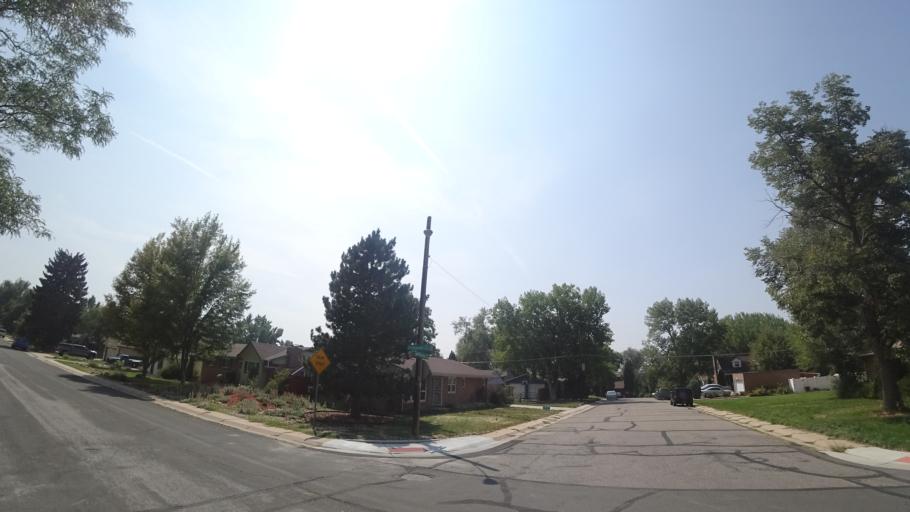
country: US
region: Colorado
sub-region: Arapahoe County
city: Englewood
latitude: 39.6404
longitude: -104.9959
